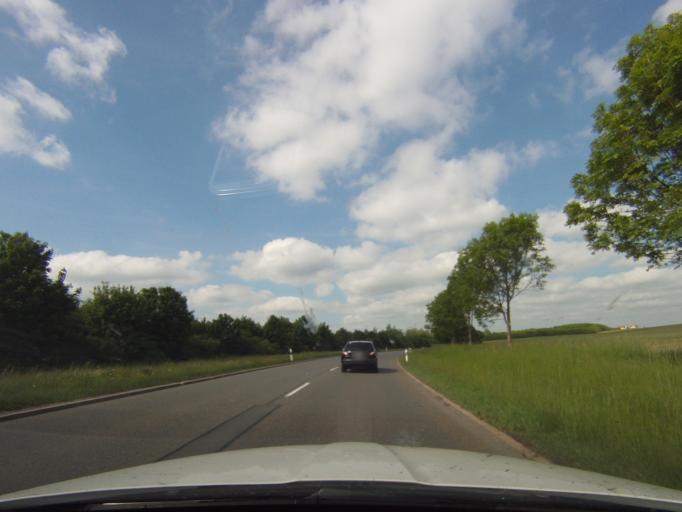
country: DE
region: Thuringia
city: Gera
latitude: 50.8699
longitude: 12.1144
